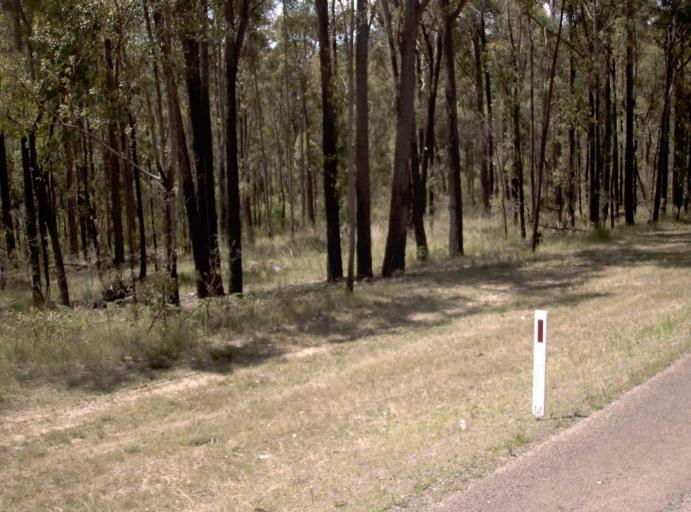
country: AU
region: New South Wales
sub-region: Bombala
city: Bombala
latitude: -37.5668
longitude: 149.1133
